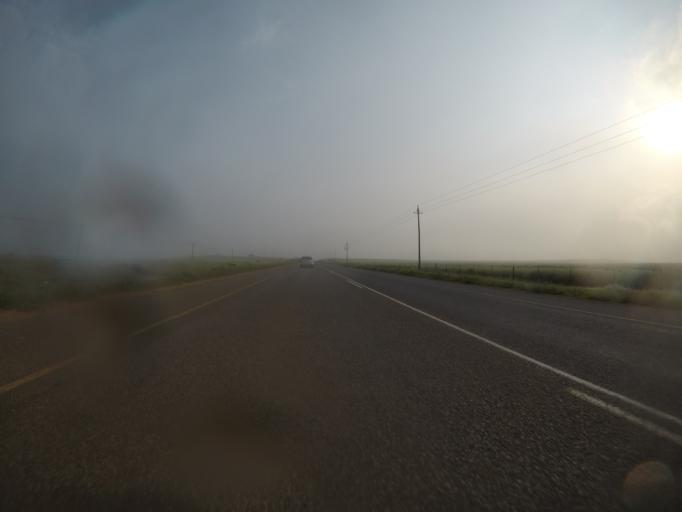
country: ZA
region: Western Cape
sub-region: City of Cape Town
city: Kraaifontein
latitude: -33.6653
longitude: 18.7077
